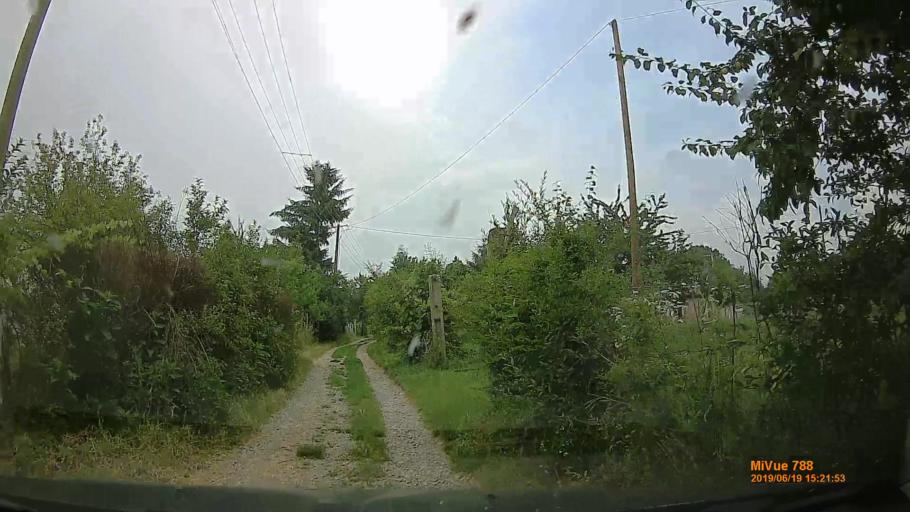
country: HU
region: Baranya
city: Szigetvar
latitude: 46.0723
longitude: 17.8470
